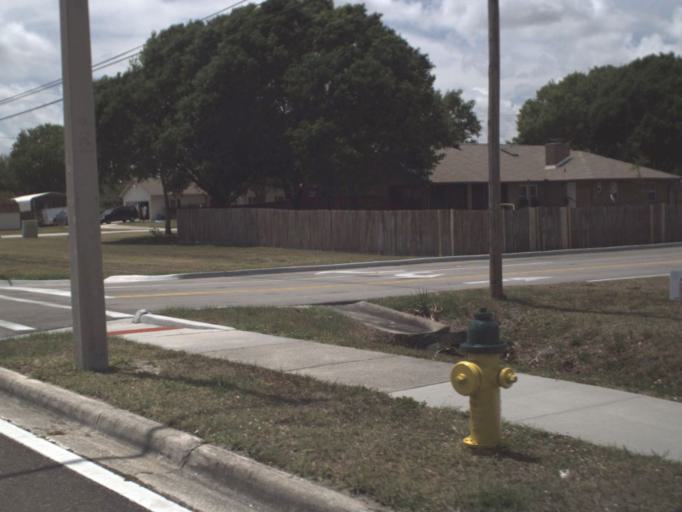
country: US
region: Florida
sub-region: Brevard County
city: Rockledge
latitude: 28.3087
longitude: -80.7429
